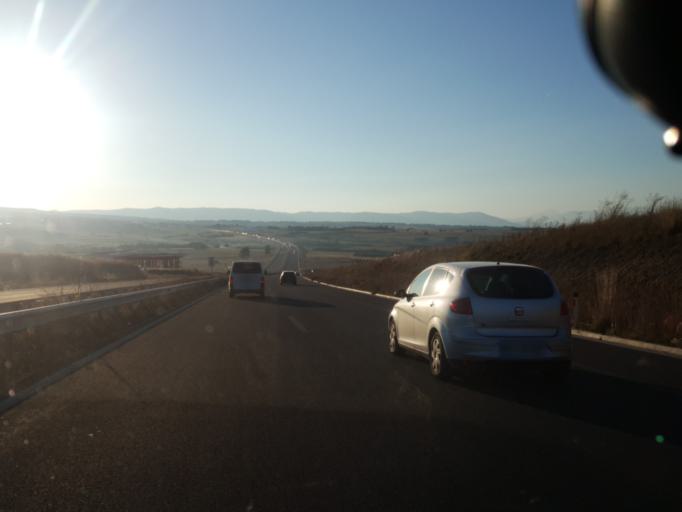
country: XK
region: Prizren
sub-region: Komuna e Malisheves
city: Llazice
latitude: 42.5744
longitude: 20.7248
